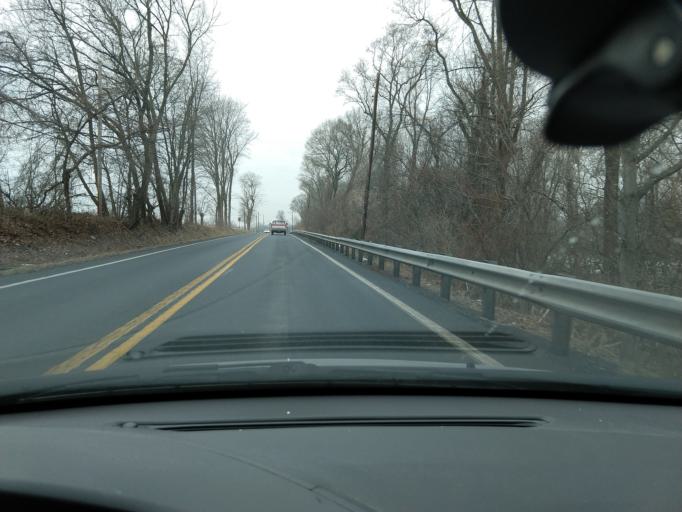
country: US
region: Pennsylvania
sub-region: Montgomery County
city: Stowe
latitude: 40.2435
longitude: -75.7037
